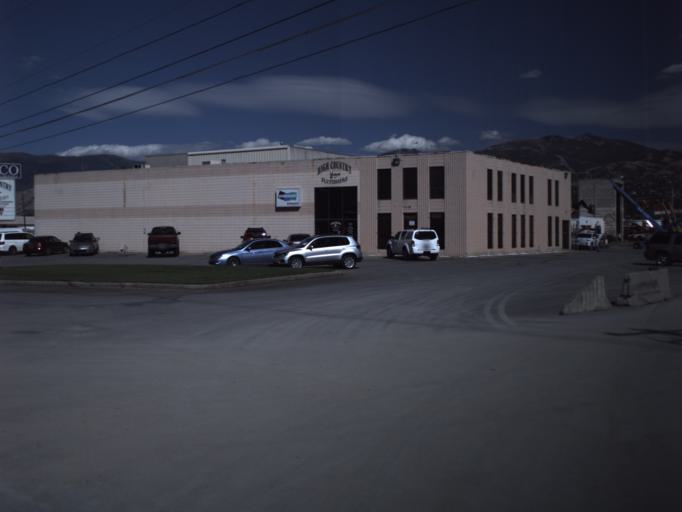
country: US
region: Utah
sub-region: Davis County
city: North Salt Lake
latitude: 40.8377
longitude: -111.9340
